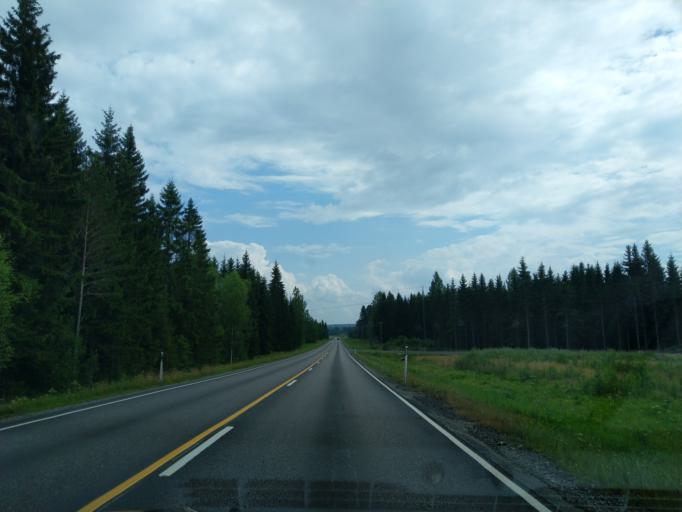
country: FI
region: South Karelia
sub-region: Imatra
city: Parikkala
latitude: 61.6123
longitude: 29.4530
